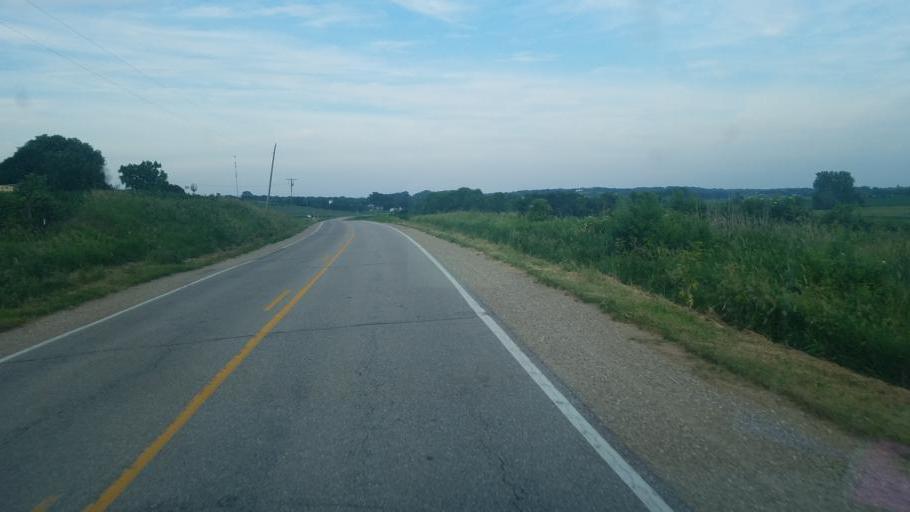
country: US
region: Iowa
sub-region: Tama County
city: Tama
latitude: 41.9610
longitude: -92.4452
